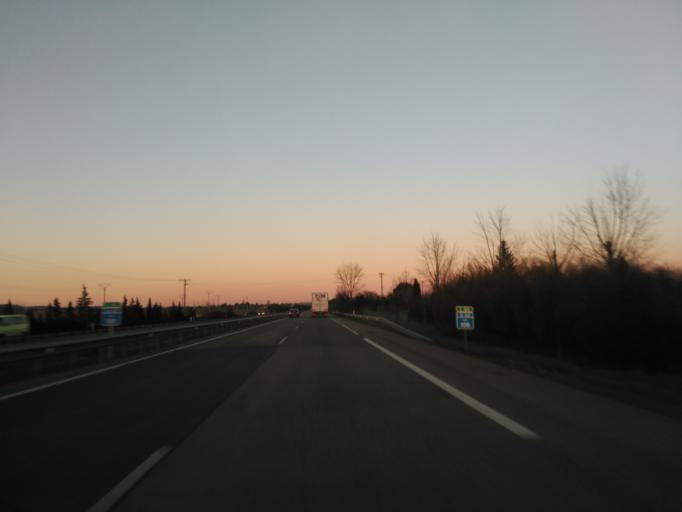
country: ES
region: Castille and Leon
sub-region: Provincia de Valladolid
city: Cubillas de Santa Marta
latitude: 41.7897
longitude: -4.6056
